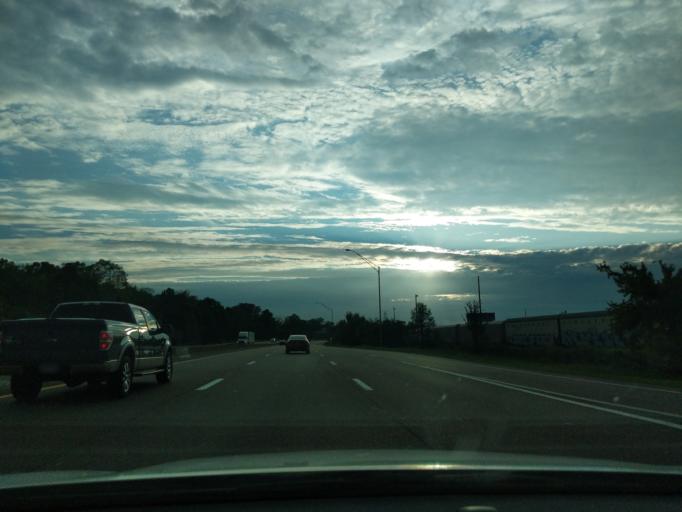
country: US
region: Tennessee
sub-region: Shelby County
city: New South Memphis
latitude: 35.0800
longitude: -90.0646
